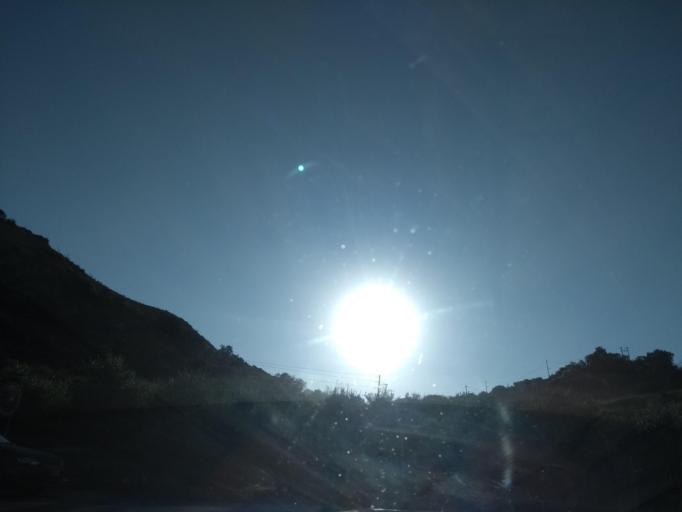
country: GR
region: Crete
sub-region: Nomos Chanias
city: Kalivai
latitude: 35.4675
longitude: 24.1529
